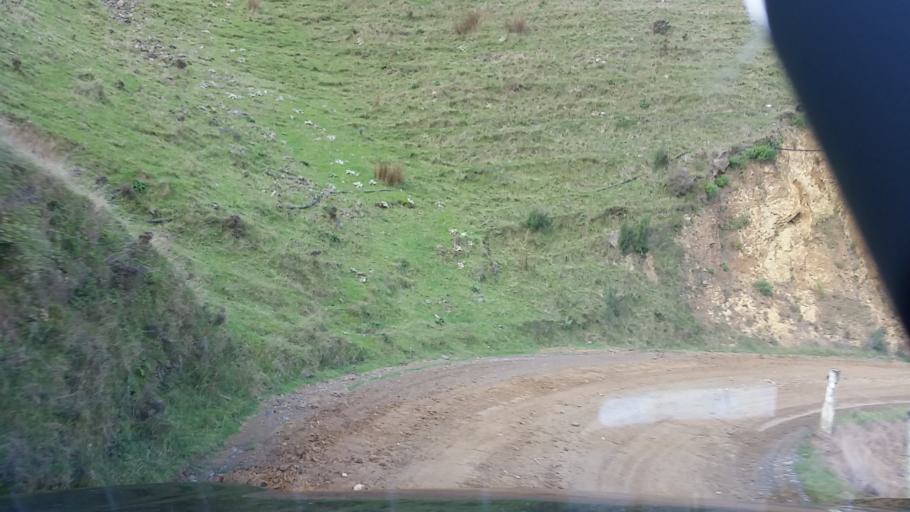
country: NZ
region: Marlborough
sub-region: Marlborough District
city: Picton
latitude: -40.9874
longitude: 173.8315
